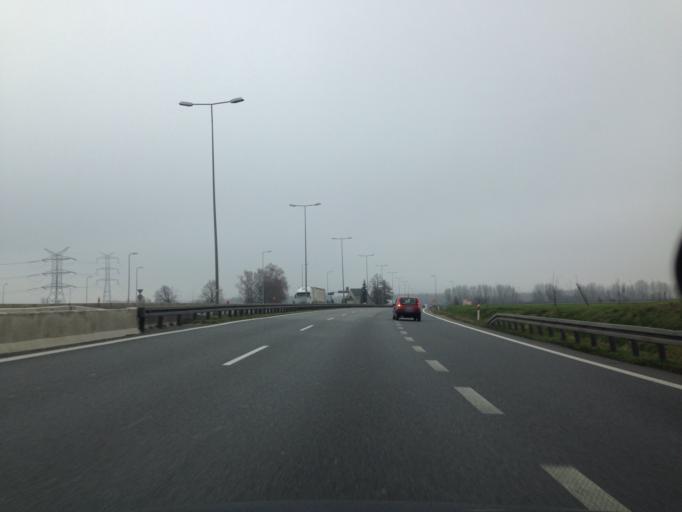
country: PL
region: Silesian Voivodeship
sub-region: Powiat bedzinski
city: Siewierz
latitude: 50.4597
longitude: 19.2315
